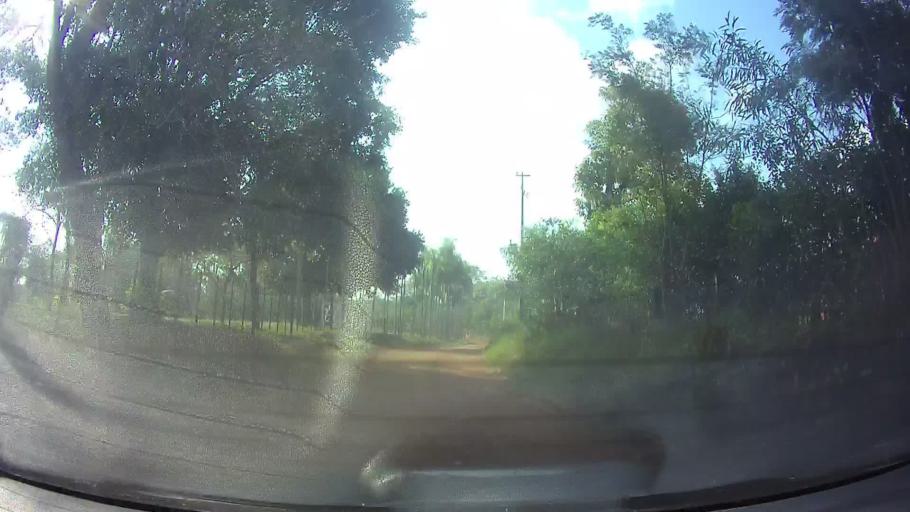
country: PY
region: Cordillera
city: Arroyos y Esteros
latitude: -25.0480
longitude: -57.1872
